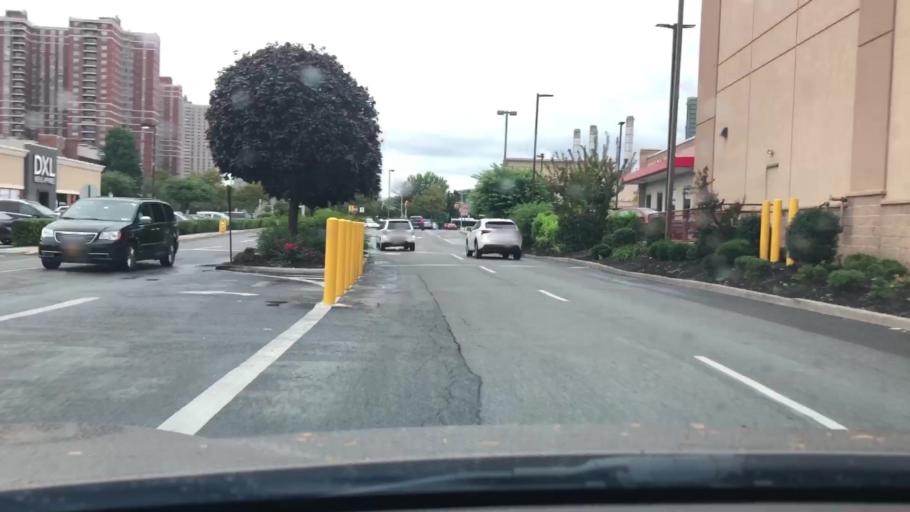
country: US
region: New York
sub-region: Bronx
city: Eastchester
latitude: 40.8680
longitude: -73.8271
